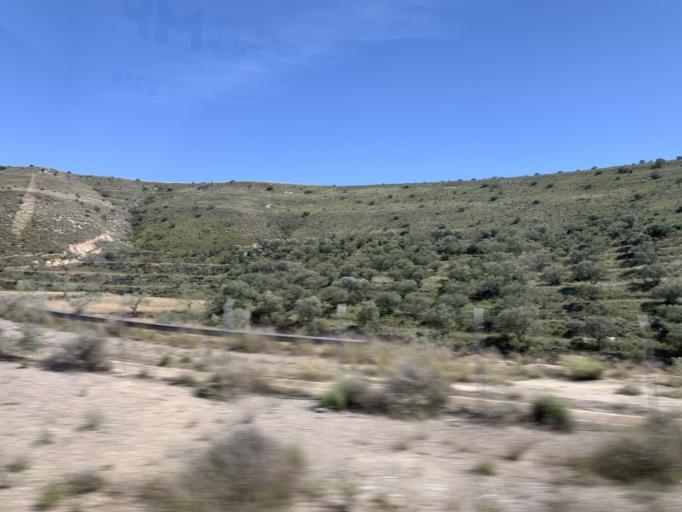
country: ES
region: Aragon
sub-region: Provincia de Huesca
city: Ballobar
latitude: 41.5949
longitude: 0.1794
